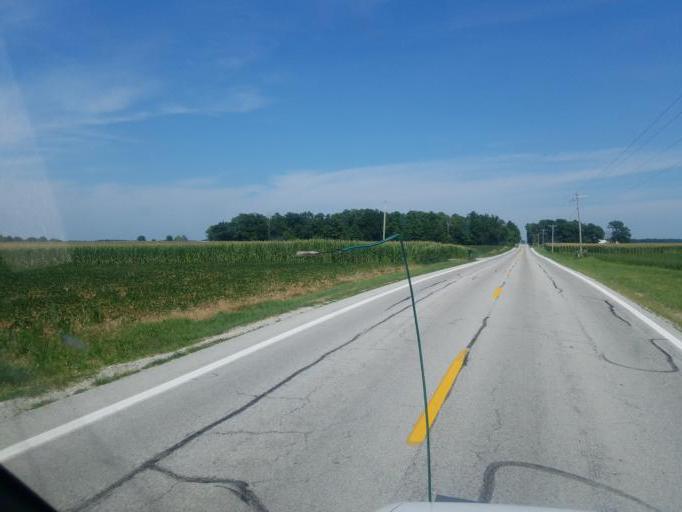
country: US
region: Ohio
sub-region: Shelby County
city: Botkins
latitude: 40.4967
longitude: -84.2253
